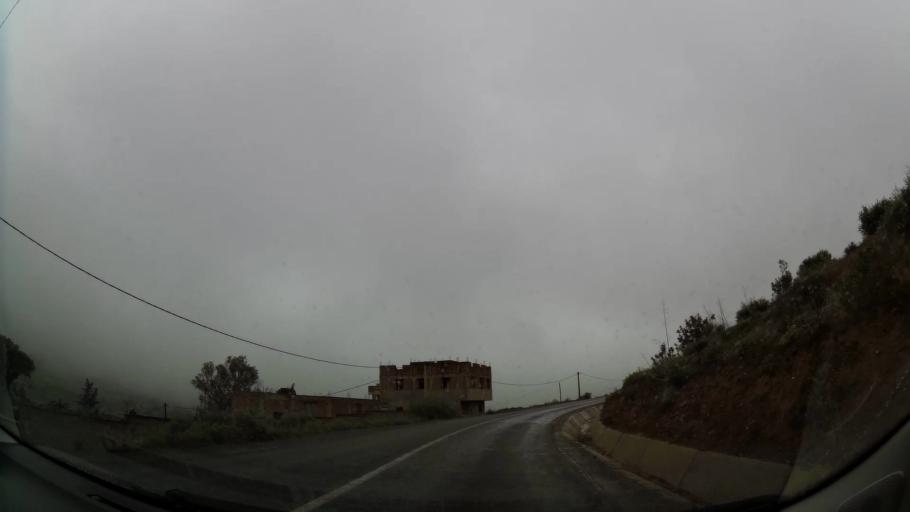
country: MA
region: Oriental
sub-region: Nador
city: Boudinar
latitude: 35.1287
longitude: -3.5864
